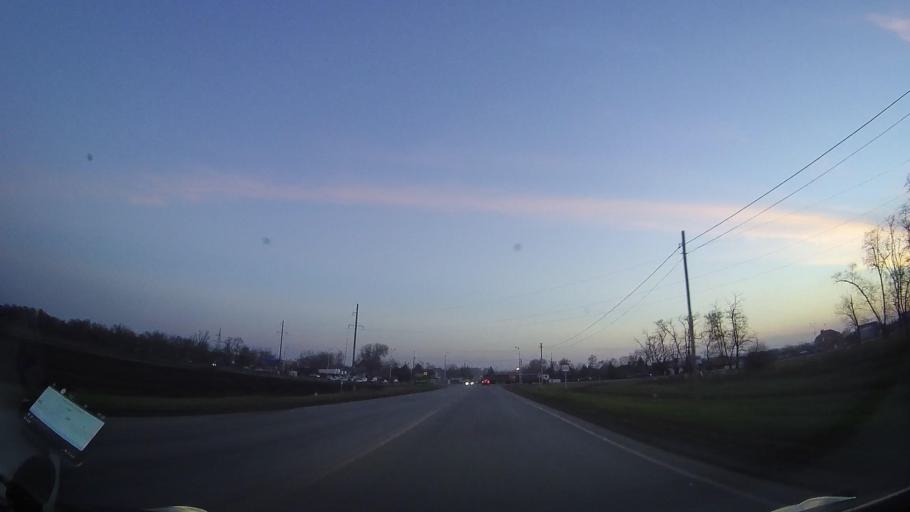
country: RU
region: Rostov
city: Zernograd
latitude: 46.8127
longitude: 40.2995
